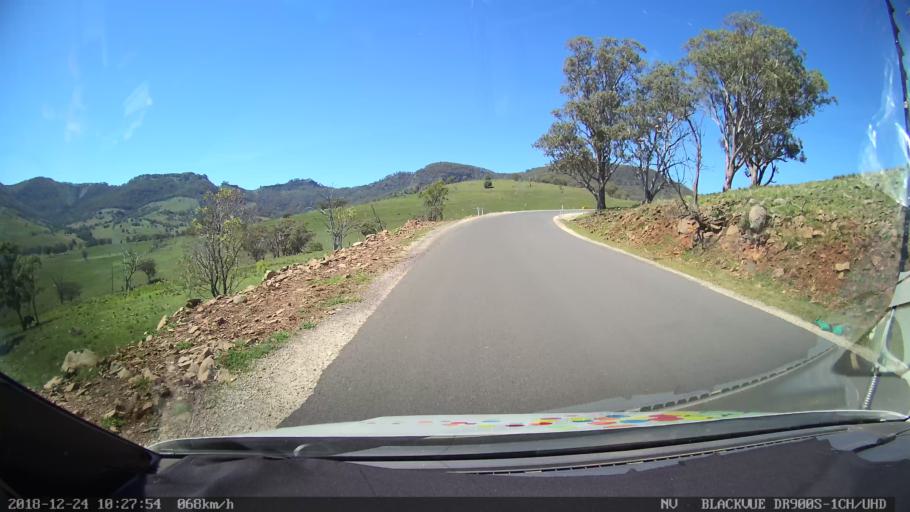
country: AU
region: New South Wales
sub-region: Liverpool Plains
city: Quirindi
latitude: -31.8224
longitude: 150.5338
